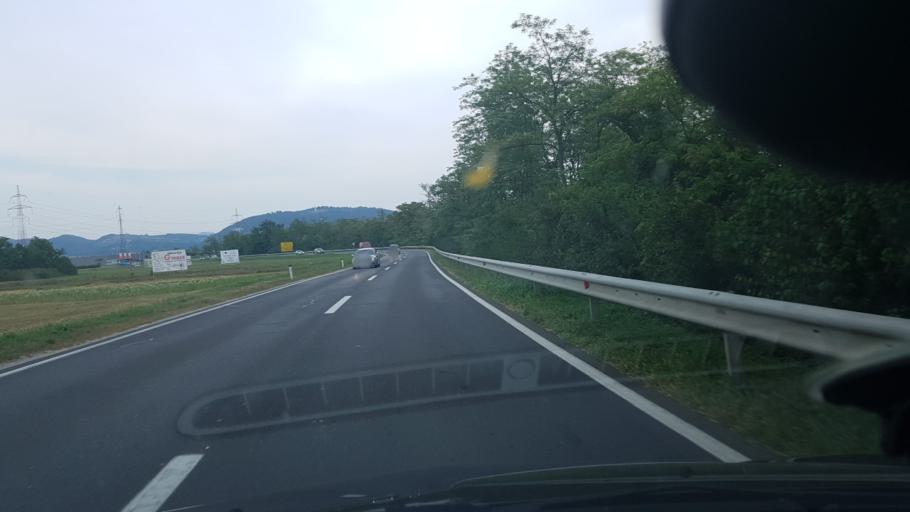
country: SI
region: Krsko
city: Leskovec pri Krskem
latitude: 45.9307
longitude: 15.4810
